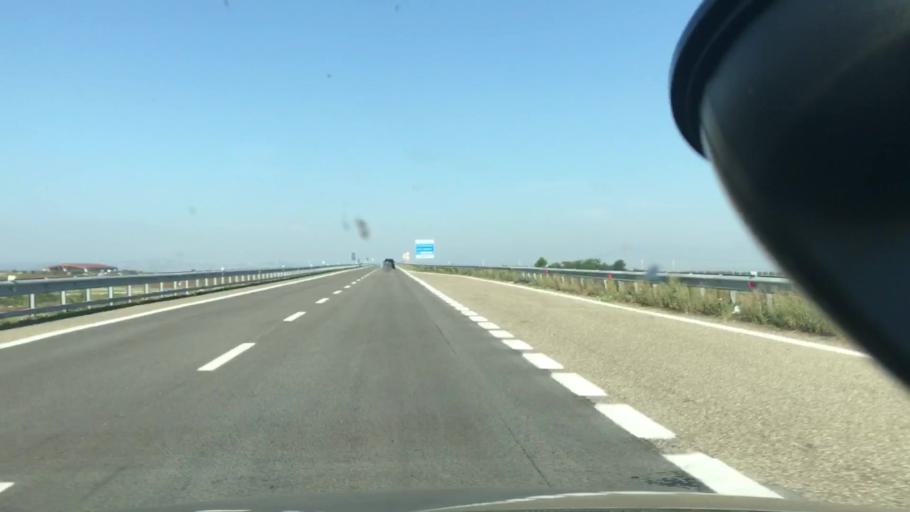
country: IT
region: Basilicate
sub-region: Provincia di Potenza
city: Montemilone
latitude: 40.9918
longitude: 15.8949
